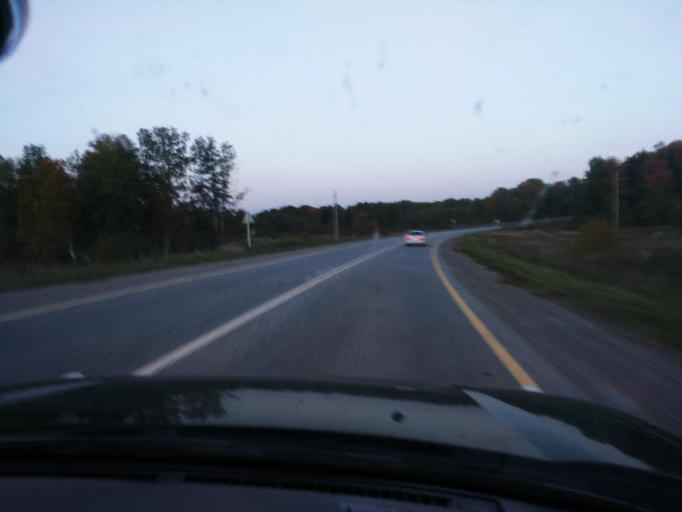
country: RU
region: Perm
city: Verkhnechusovskiye Gorodki
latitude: 58.2936
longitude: 56.8886
